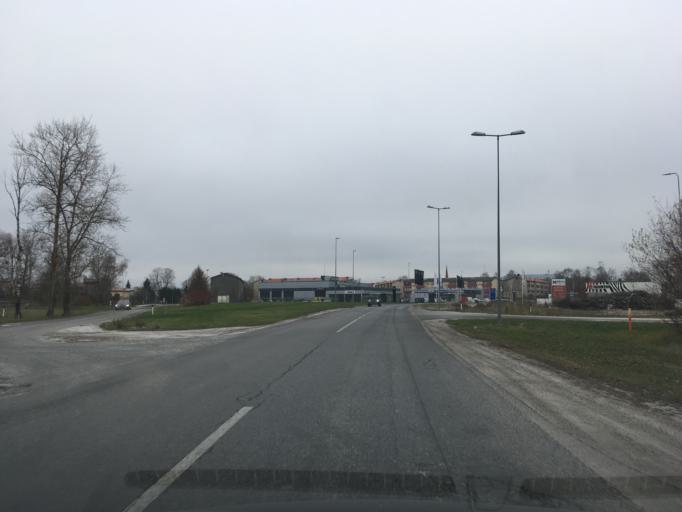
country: EE
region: Ida-Virumaa
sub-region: Johvi vald
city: Johvi
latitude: 59.3666
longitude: 27.4170
